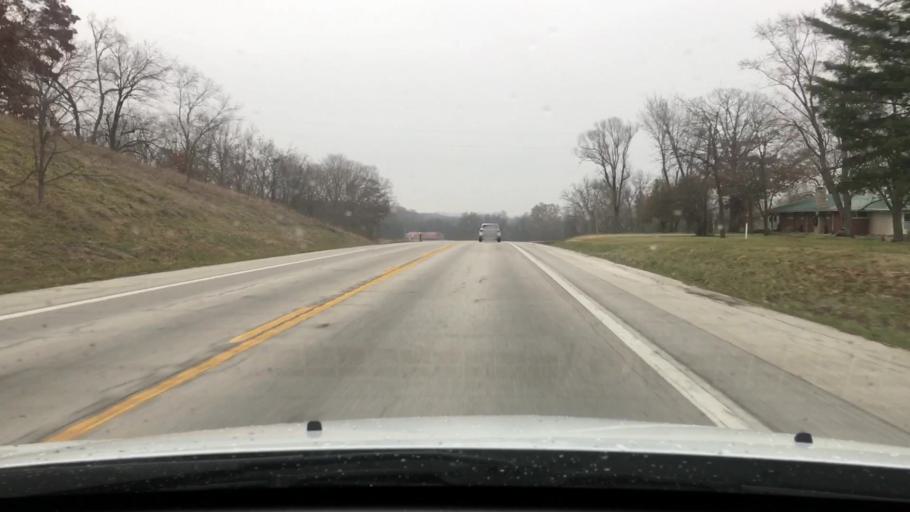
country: US
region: Missouri
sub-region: Pike County
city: Bowling Green
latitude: 39.3775
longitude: -91.1545
